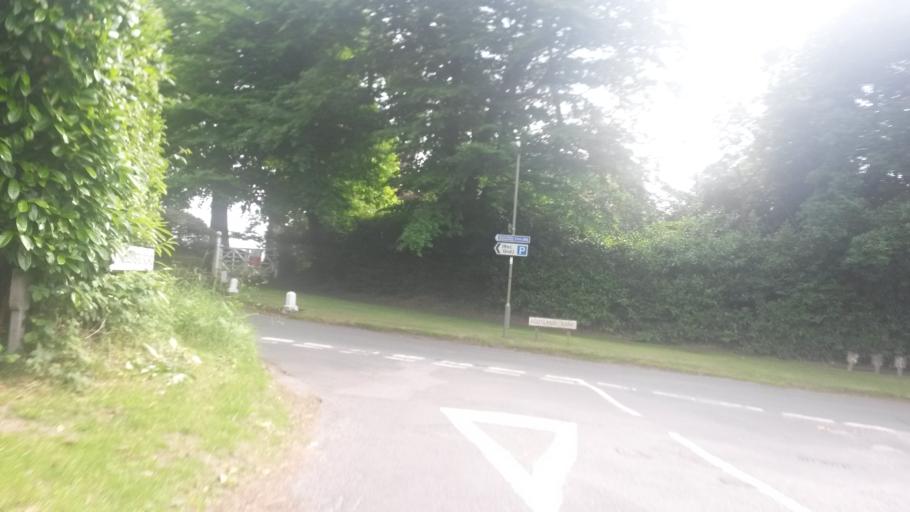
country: GB
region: England
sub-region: Surrey
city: Haslemere
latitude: 51.0821
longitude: -0.7103
